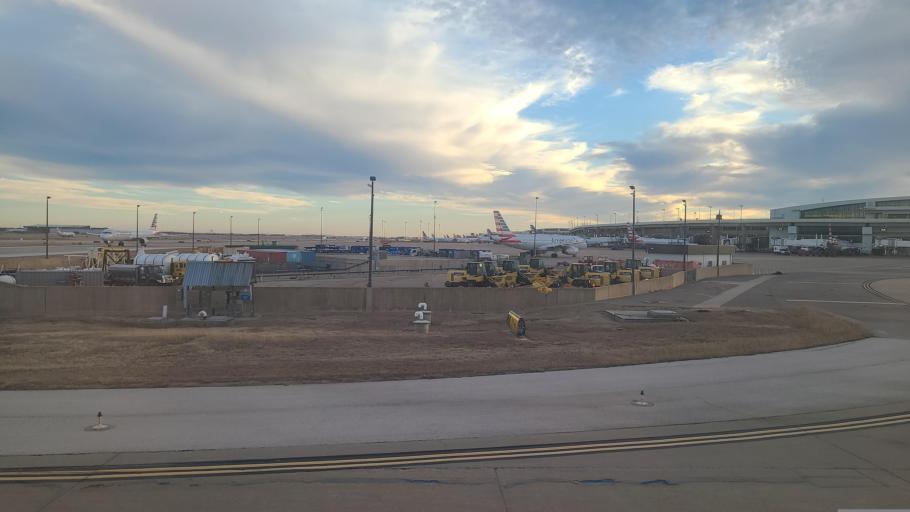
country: US
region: Texas
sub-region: Dallas County
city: Coppell
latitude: 32.9090
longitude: -97.0341
